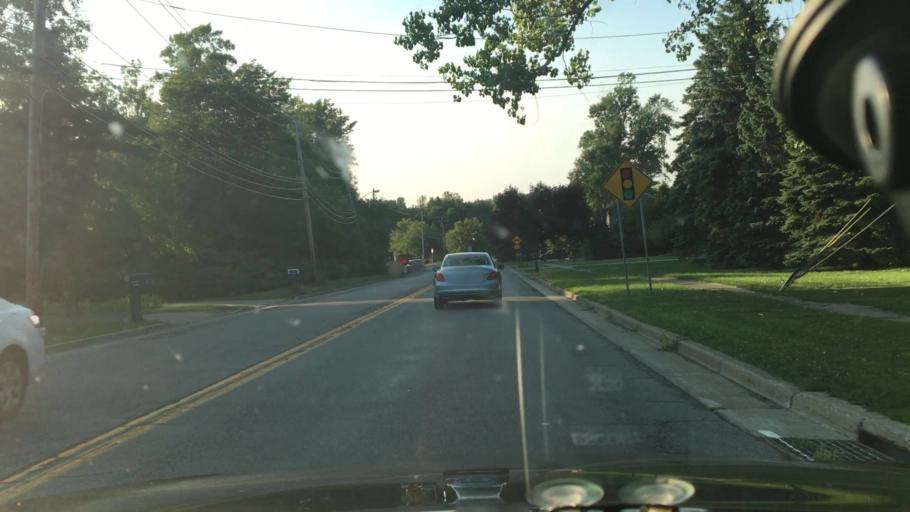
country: US
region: New York
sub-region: Erie County
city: Amherst
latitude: 43.0053
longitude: -78.7632
